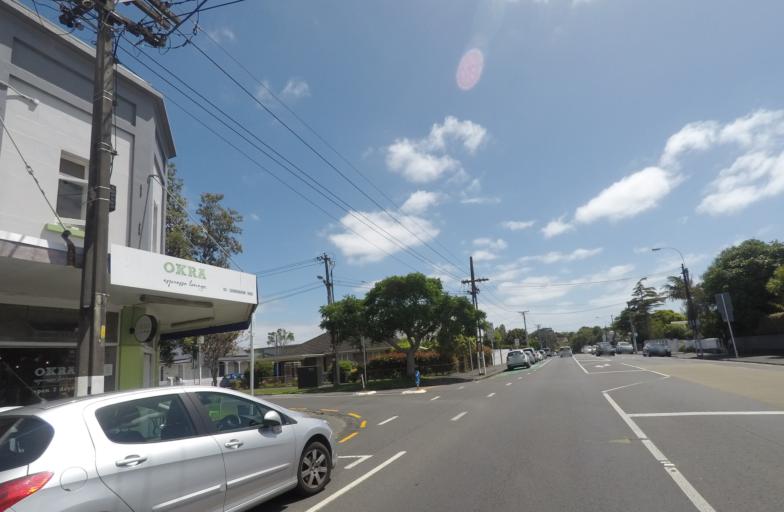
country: NZ
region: Auckland
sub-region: Auckland
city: Auckland
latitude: -36.8777
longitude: 174.7408
